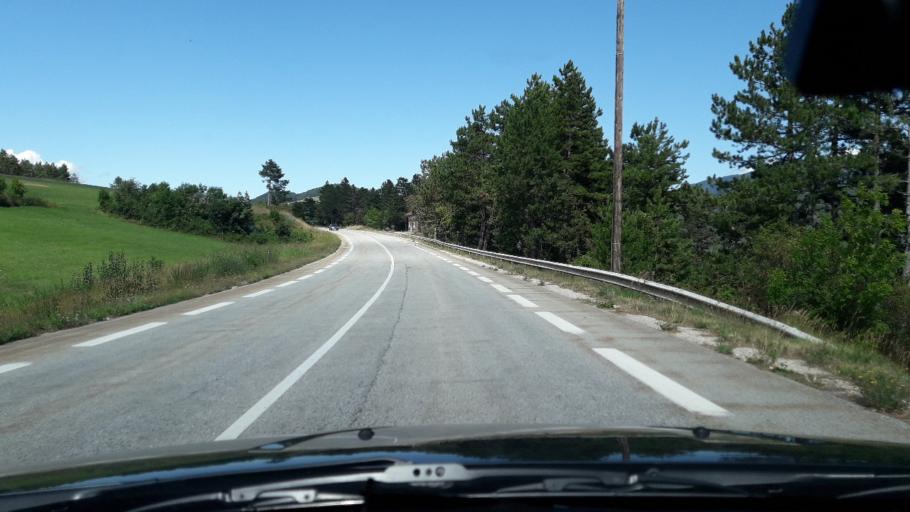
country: FR
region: Rhone-Alpes
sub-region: Departement de l'Isere
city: La Motte-Saint-Martin
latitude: 44.8739
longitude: 5.6246
